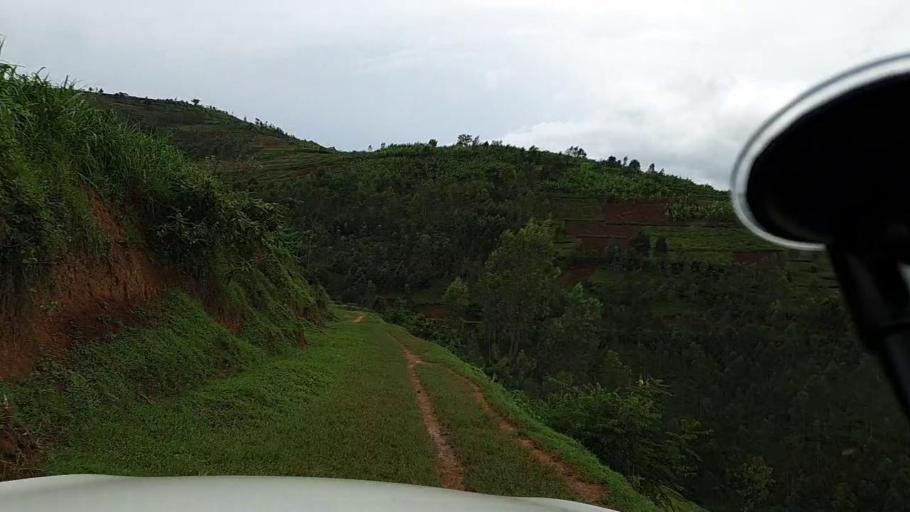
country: RW
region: Southern Province
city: Gitarama
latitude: -2.0748
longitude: 29.6428
